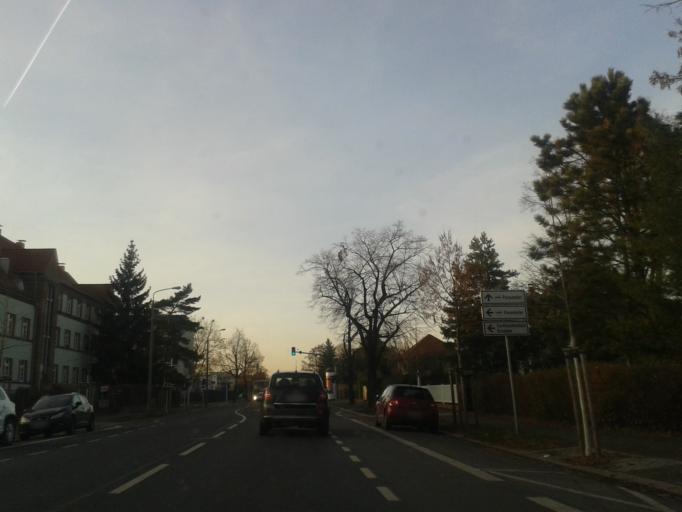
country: DE
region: Saxony
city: Dresden
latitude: 51.0274
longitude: 13.7892
